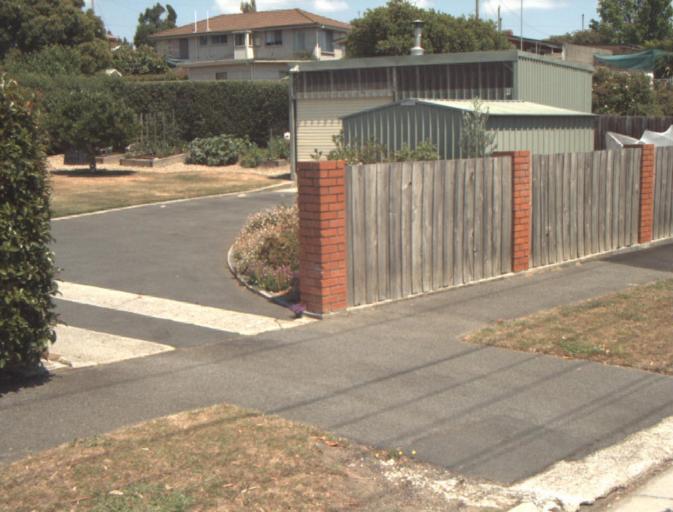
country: AU
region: Tasmania
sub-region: Launceston
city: Summerhill
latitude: -41.4856
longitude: 147.1742
